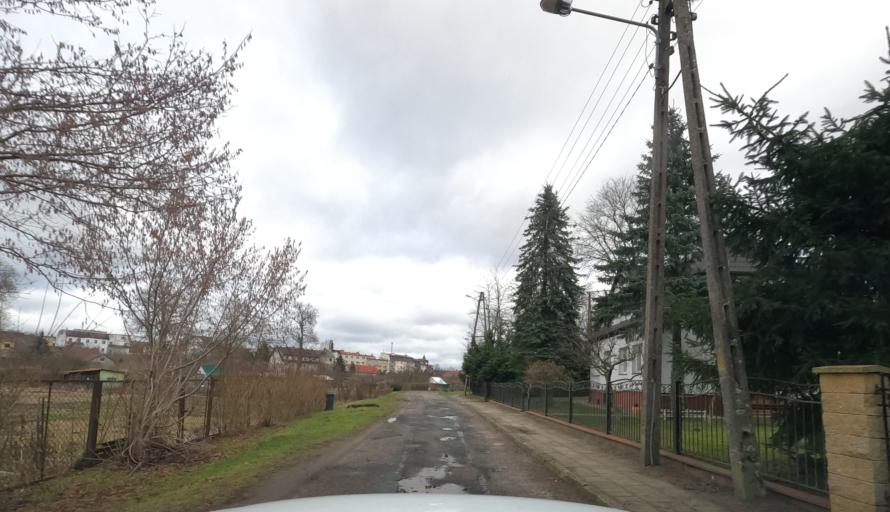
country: PL
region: West Pomeranian Voivodeship
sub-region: Powiat choszczenski
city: Recz
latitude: 53.2573
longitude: 15.5468
